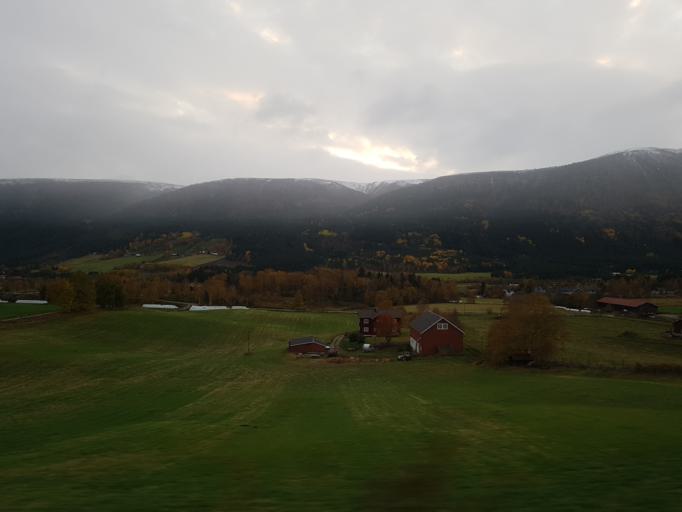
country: NO
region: Oppland
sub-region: Dovre
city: Dovre
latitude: 61.9933
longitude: 9.2398
